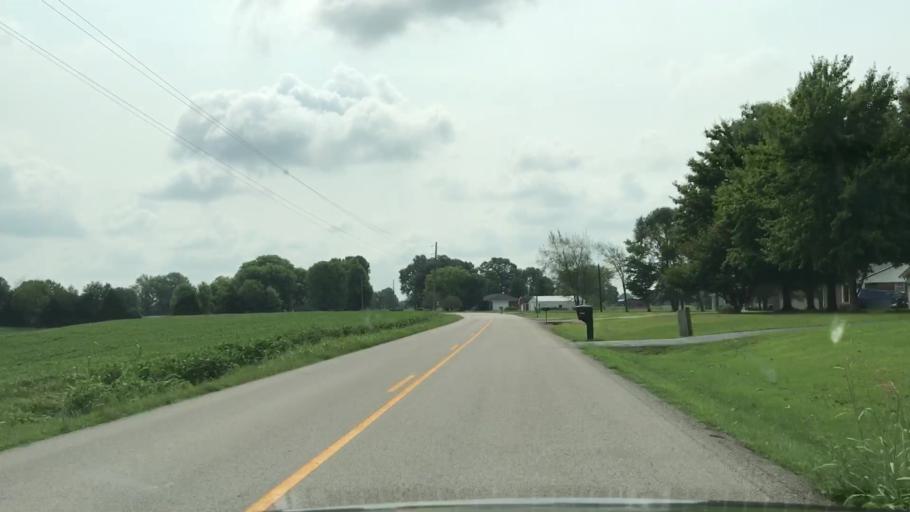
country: US
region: Kentucky
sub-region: Edmonson County
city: Brownsville
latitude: 37.1349
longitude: -86.1741
